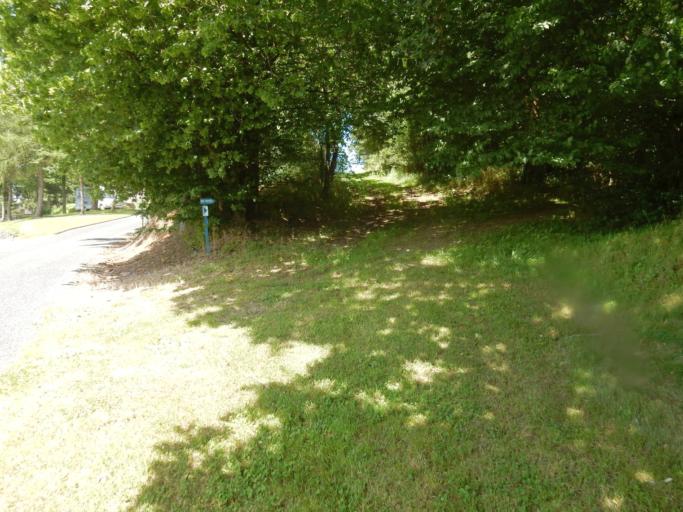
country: LU
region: Diekirch
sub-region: Canton de Diekirch
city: Bourscheid
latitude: 49.9336
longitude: 6.0628
